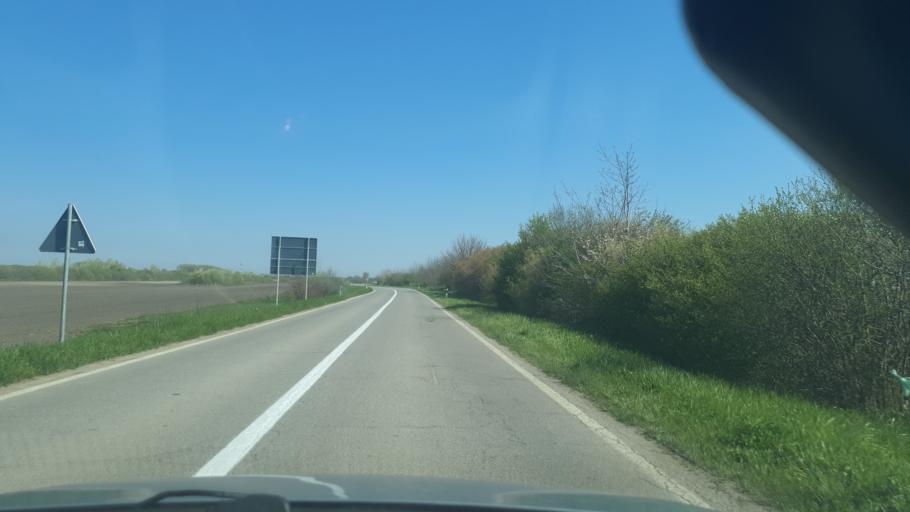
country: RS
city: Kolut
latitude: 45.8666
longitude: 18.9340
